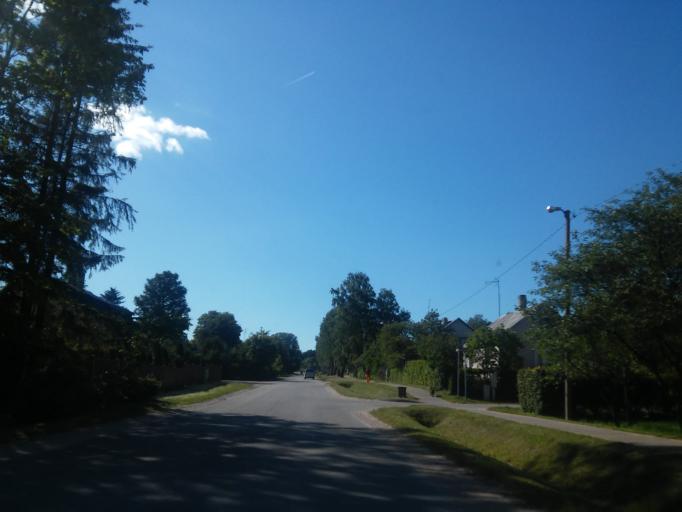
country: LV
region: Vainode
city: Vainode
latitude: 56.4164
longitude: 21.8484
